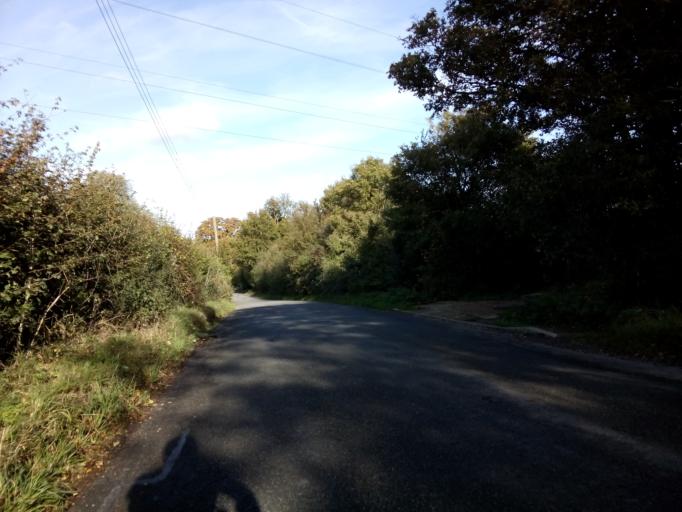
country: GB
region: England
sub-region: Suffolk
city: Capel Saint Mary
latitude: 52.0390
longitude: 1.0276
